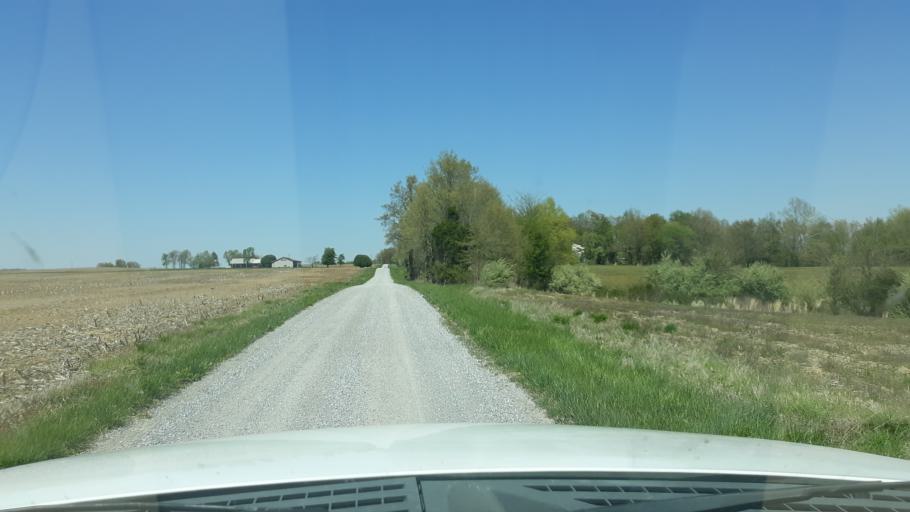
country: US
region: Illinois
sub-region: Saline County
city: Harrisburg
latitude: 37.8784
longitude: -88.6421
